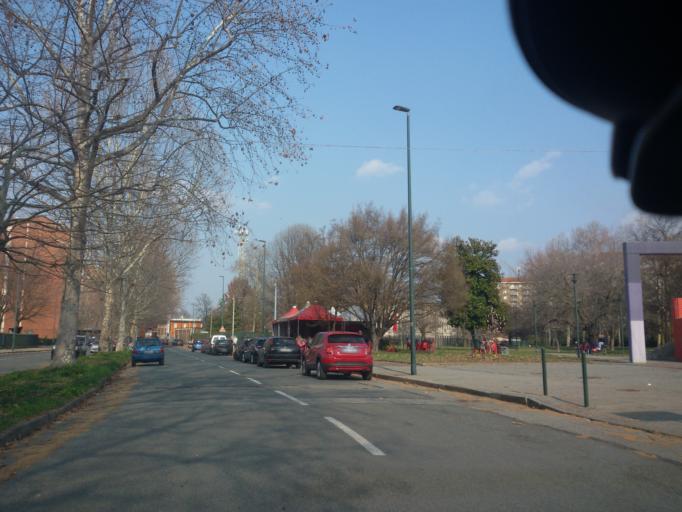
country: IT
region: Piedmont
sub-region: Provincia di Torino
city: Savonera
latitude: 45.1007
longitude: 7.6342
